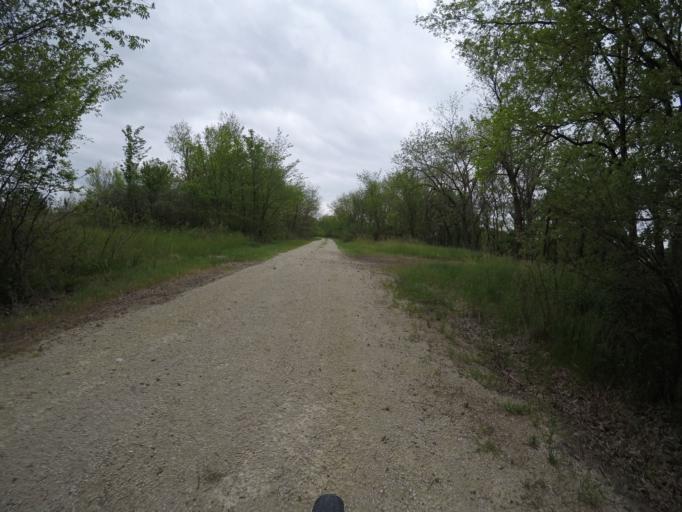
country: US
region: Nebraska
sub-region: Gage County
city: Wymore
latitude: 40.1048
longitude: -96.6151
